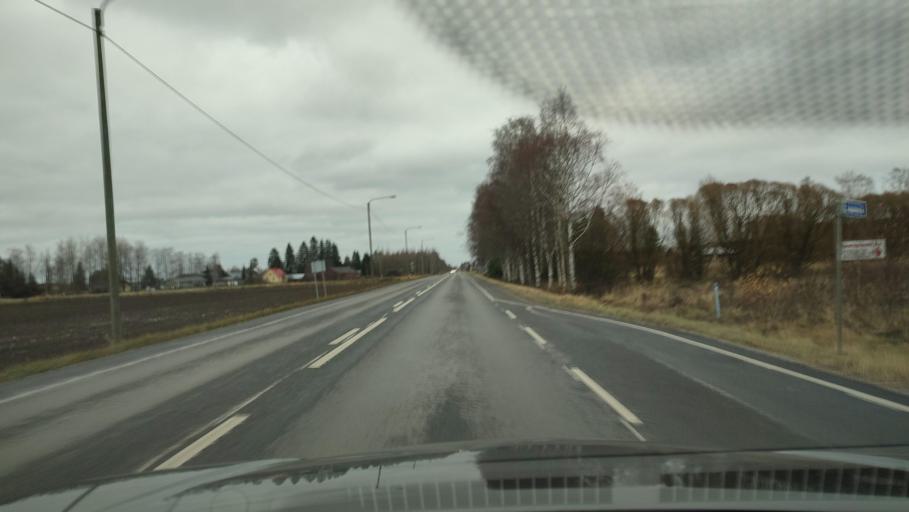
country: FI
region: Southern Ostrobothnia
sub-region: Seinaejoki
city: Ilmajoki
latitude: 62.6931
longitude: 22.4986
